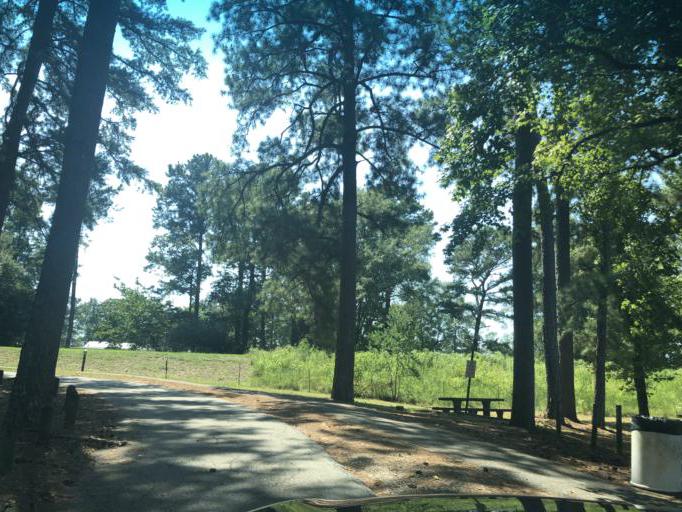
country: US
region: Georgia
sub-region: Muscogee County
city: Columbus
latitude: 32.5099
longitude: -84.9146
